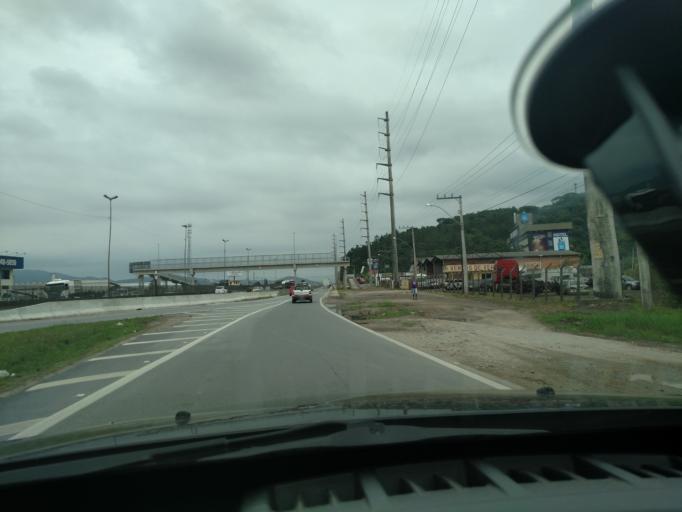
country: BR
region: Santa Catarina
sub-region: Itajai
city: Itajai
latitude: -26.8926
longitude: -48.7207
